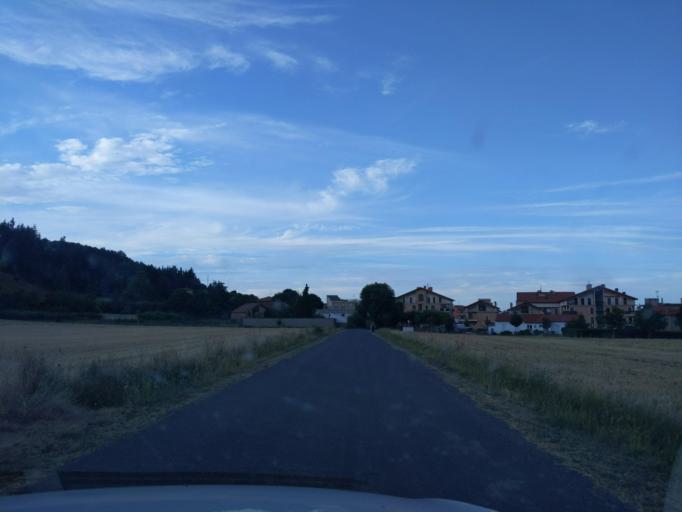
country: ES
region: La Rioja
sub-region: Provincia de La Rioja
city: Santurdejo
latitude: 42.3886
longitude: -2.9820
